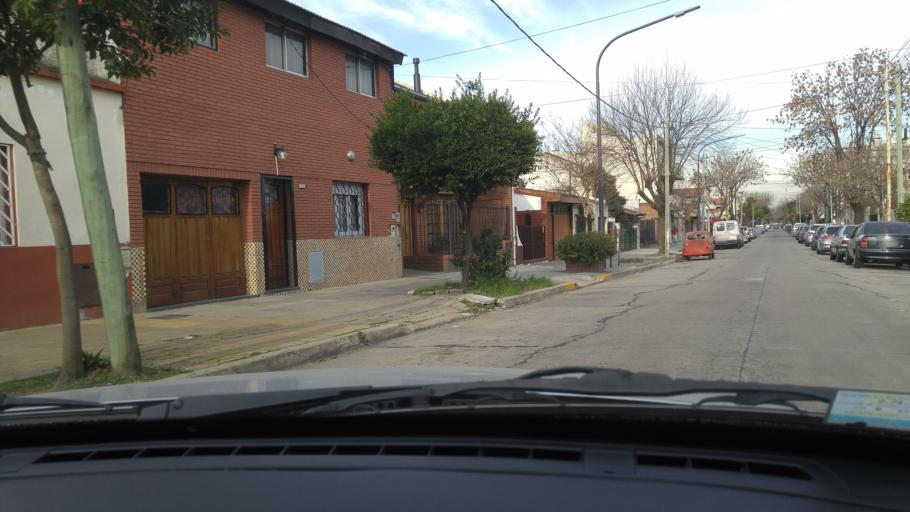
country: AR
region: Buenos Aires F.D.
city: Villa Santa Rita
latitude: -34.6268
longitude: -58.5164
